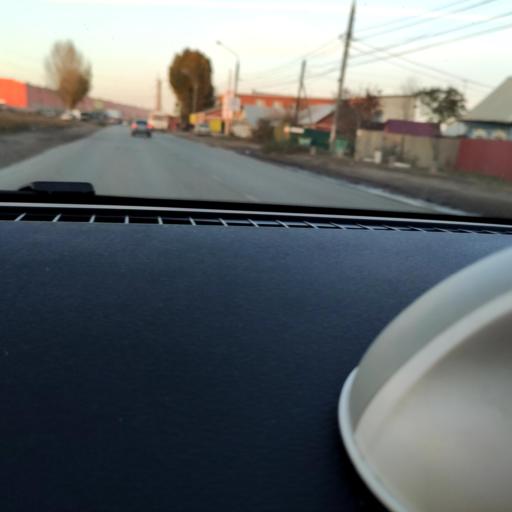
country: RU
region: Samara
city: Petra-Dubrava
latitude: 53.2518
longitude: 50.3102
